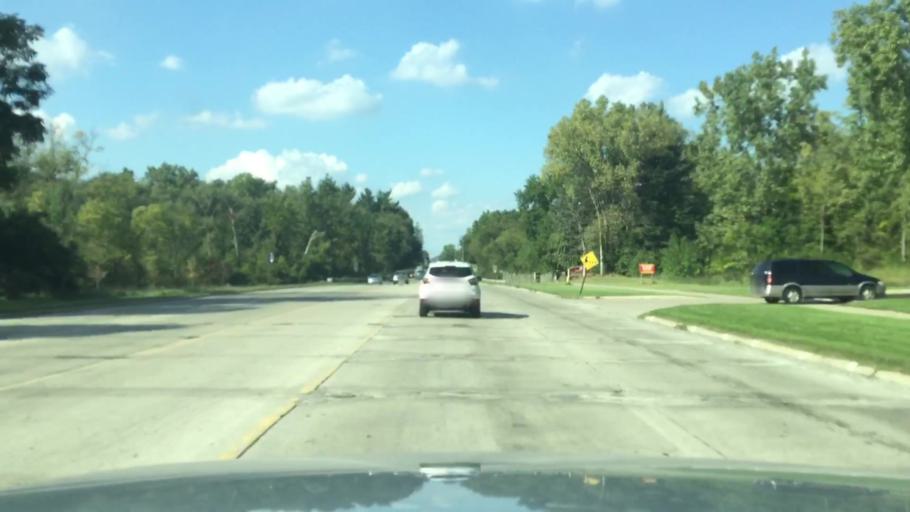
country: US
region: Michigan
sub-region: Wayne County
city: Westland
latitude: 42.3349
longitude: -83.4091
